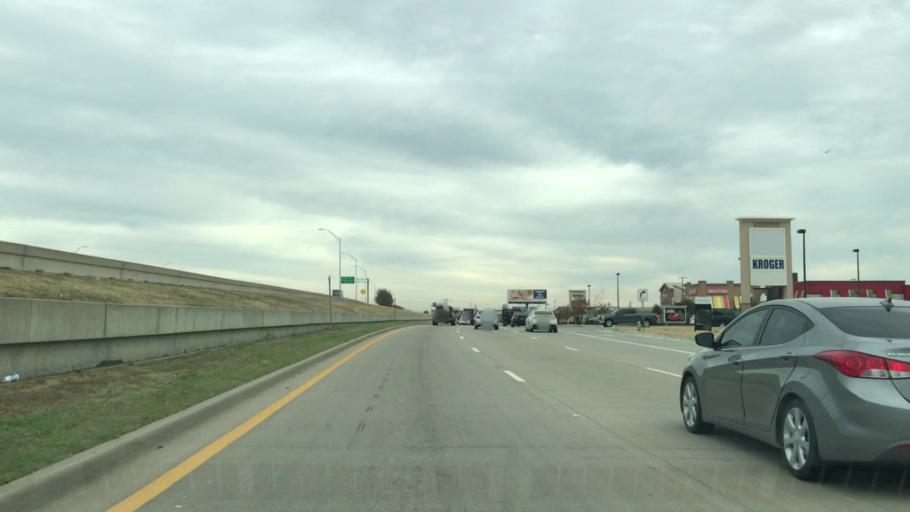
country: US
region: Texas
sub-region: Denton County
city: The Colony
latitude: 33.0637
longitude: -96.8926
